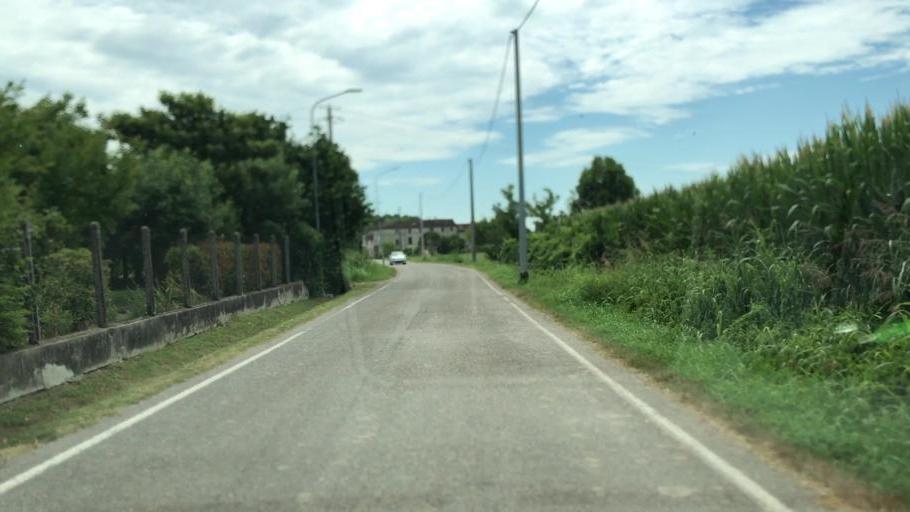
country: IT
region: Lombardy
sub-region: Provincia di Mantova
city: Ceresara
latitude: 45.2672
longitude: 10.5762
